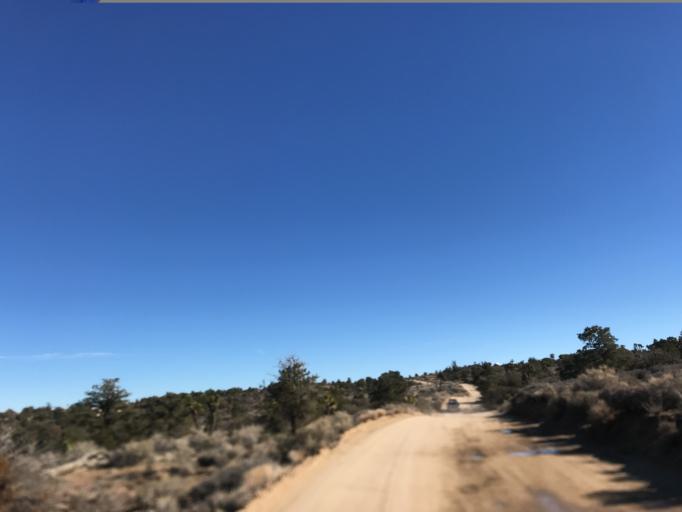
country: US
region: California
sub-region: San Bernardino County
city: Morongo Valley
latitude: 34.2162
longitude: -116.6155
